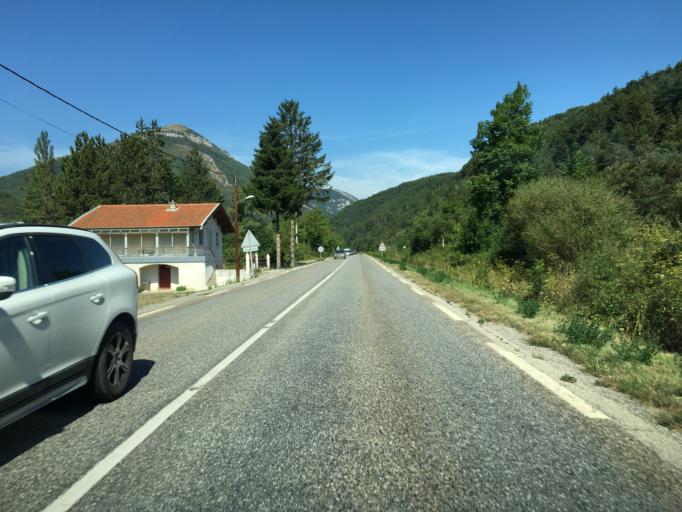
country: FR
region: Provence-Alpes-Cote d'Azur
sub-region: Departement des Hautes-Alpes
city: Veynes
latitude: 44.5698
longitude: 5.7358
